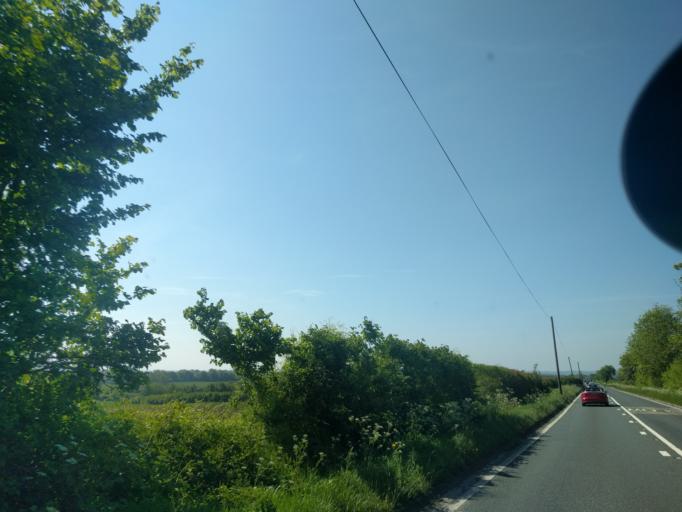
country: GB
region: England
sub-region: Somerset
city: Ilchester
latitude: 51.0391
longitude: -2.6556
